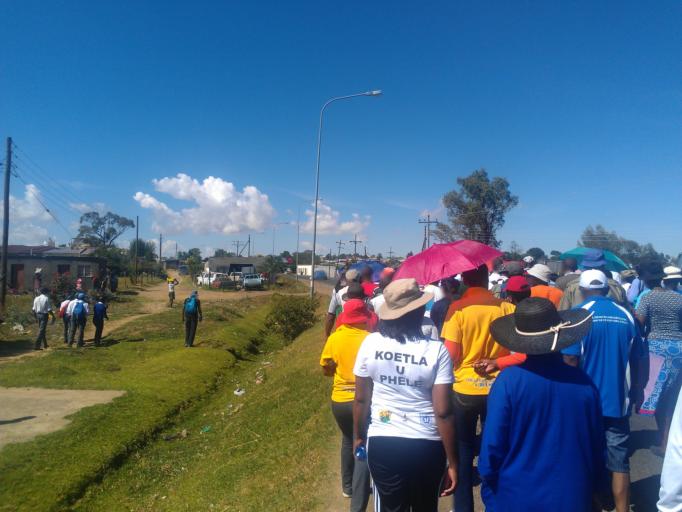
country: LS
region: Berea
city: Teyateyaneng
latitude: -29.1442
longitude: 27.7495
